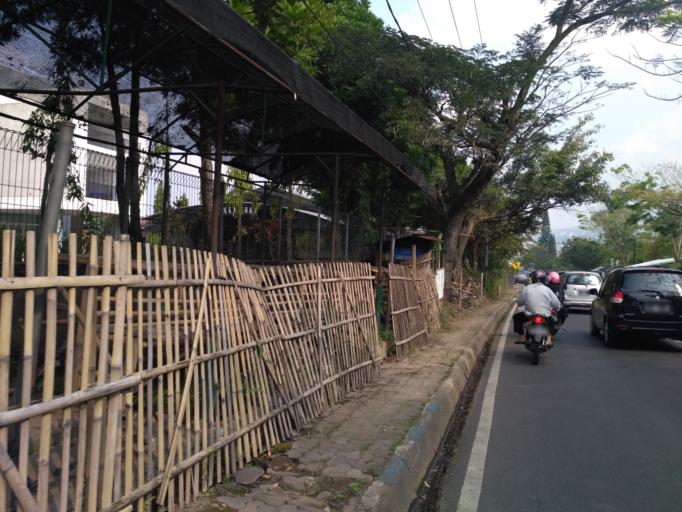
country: ID
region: East Java
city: Batu
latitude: -7.8595
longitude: 112.5269
